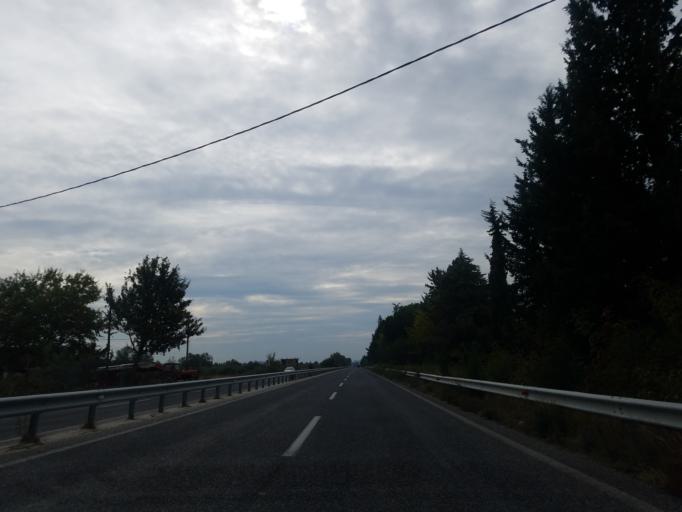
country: GR
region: Thessaly
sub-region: Trikala
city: Vasiliki
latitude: 39.6431
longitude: 21.6915
